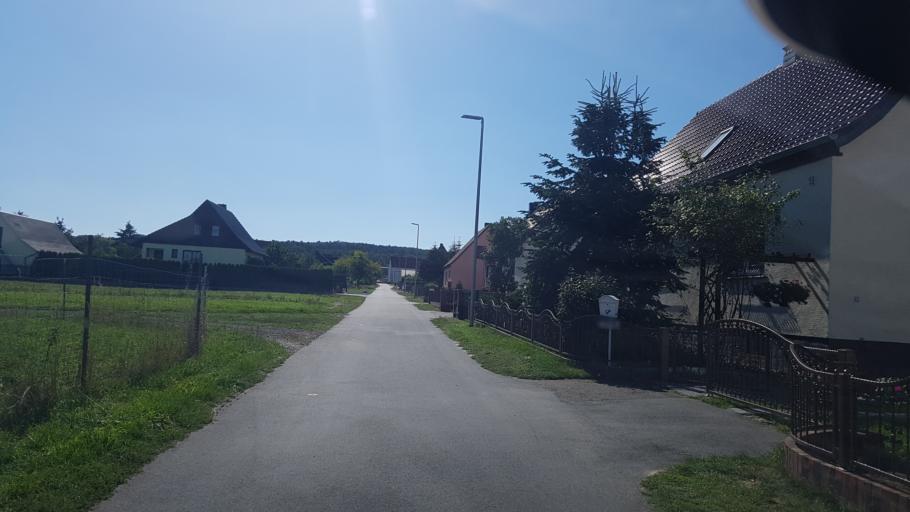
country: DE
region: Brandenburg
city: Hirschfeld
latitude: 51.3902
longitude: 13.6164
